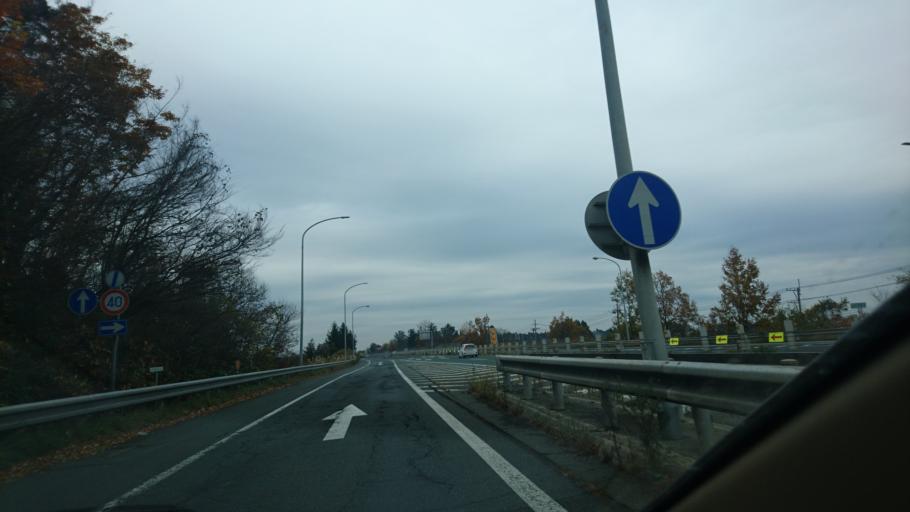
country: JP
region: Iwate
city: Kitakami
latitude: 39.2436
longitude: 141.0792
